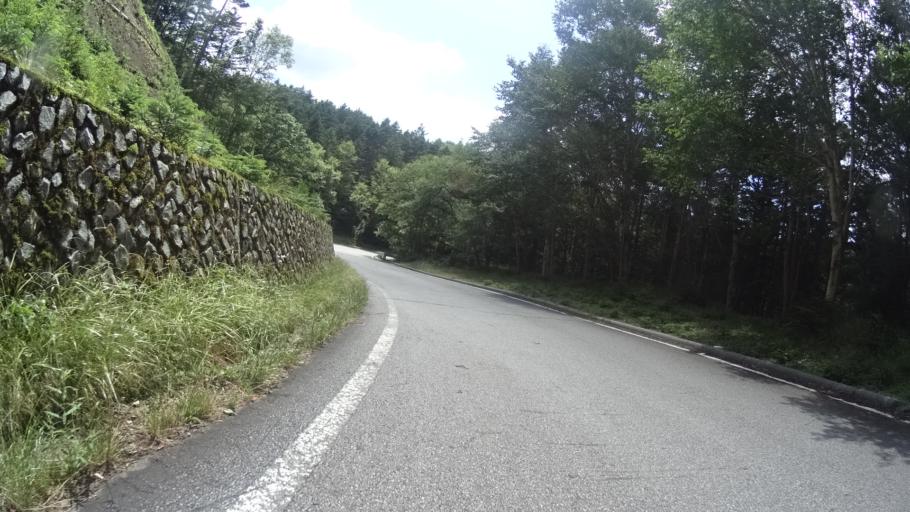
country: JP
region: Yamanashi
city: Enzan
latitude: 35.8581
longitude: 138.6480
